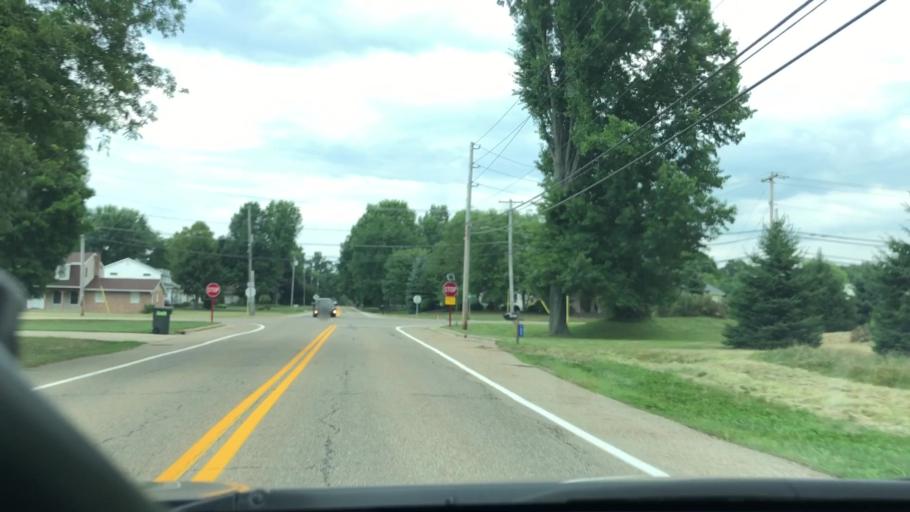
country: US
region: Ohio
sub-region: Summit County
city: New Franklin
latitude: 40.8942
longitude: -81.5179
